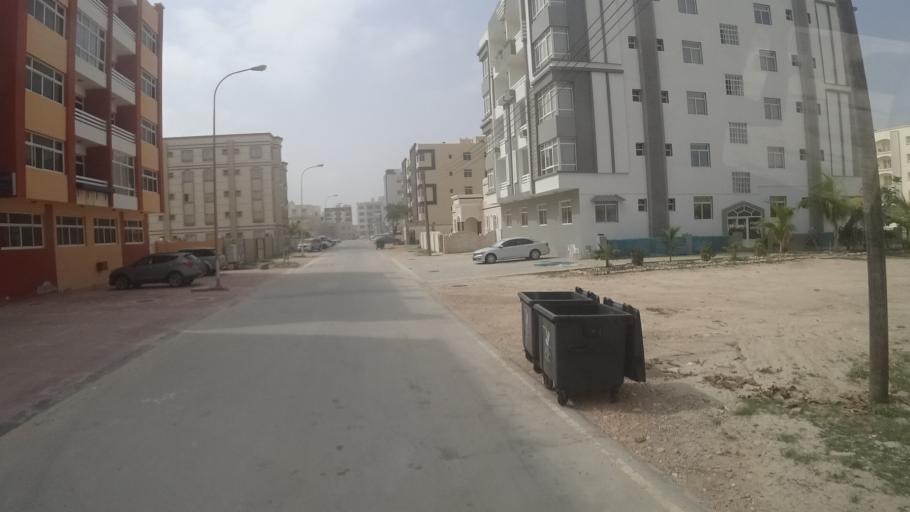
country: OM
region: Zufar
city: Salalah
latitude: 17.0120
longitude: 54.1736
